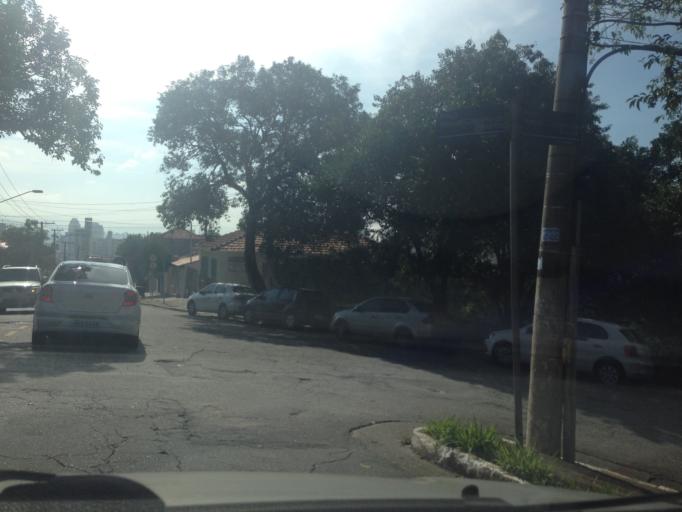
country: BR
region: Sao Paulo
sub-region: Sao Paulo
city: Sao Paulo
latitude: -23.5314
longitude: -46.7095
